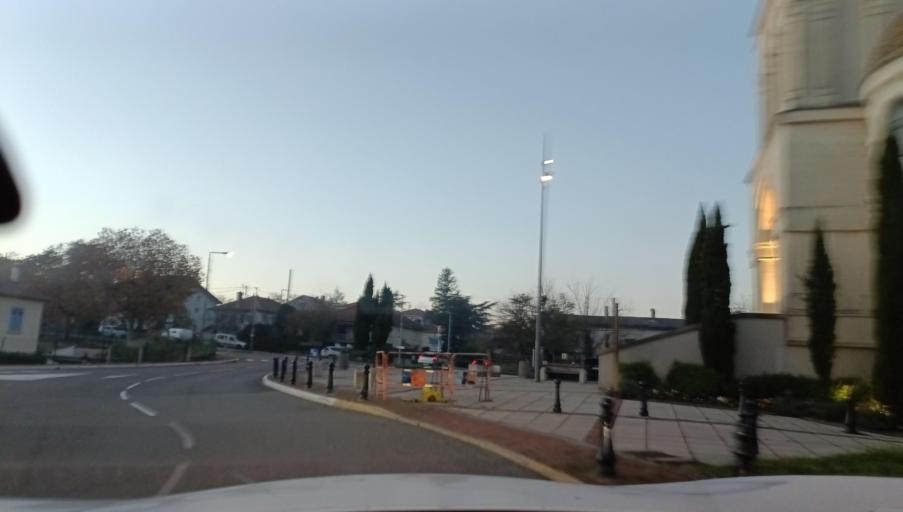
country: FR
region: Rhone-Alpes
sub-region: Departement de l'Isere
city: Chasse-sur-Rhone
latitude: 45.5808
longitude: 4.8050
